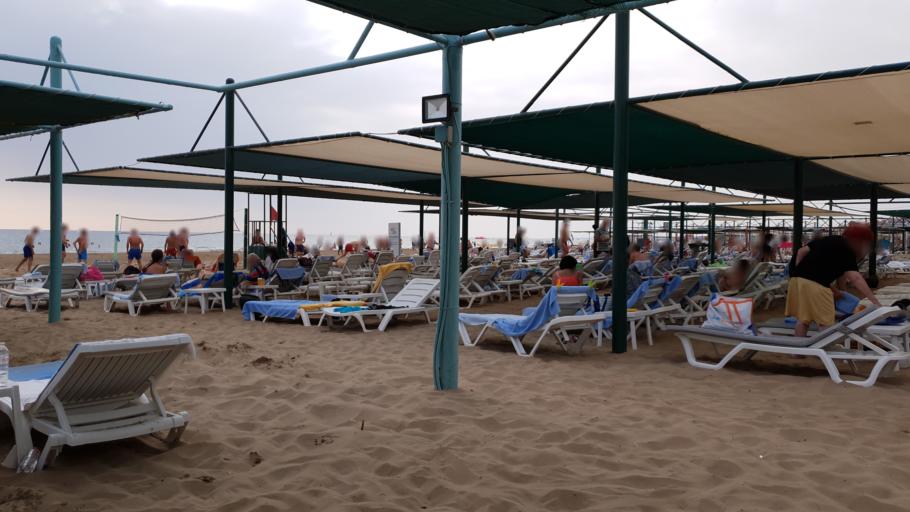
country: TR
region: Antalya
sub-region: Manavgat
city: Side
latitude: 36.7958
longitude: 31.3660
